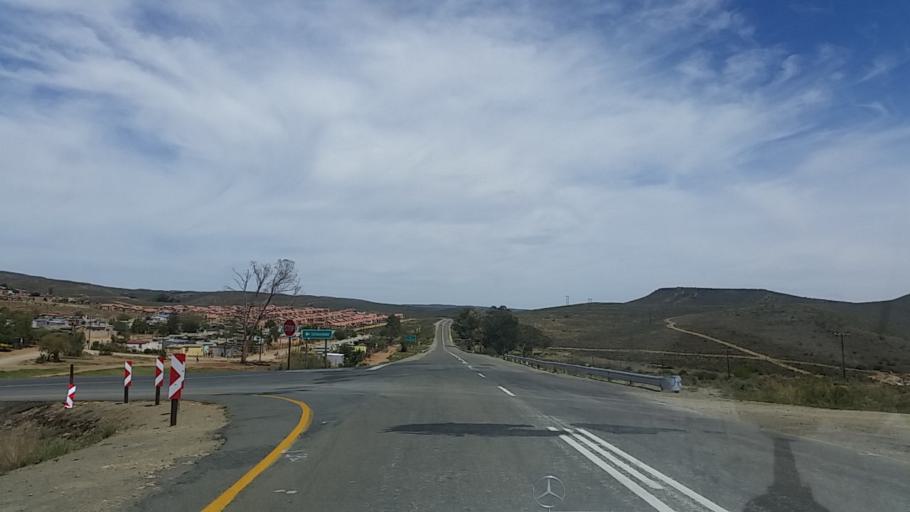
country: ZA
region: Western Cape
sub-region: Eden District Municipality
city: Knysna
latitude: -33.6607
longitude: 23.1115
